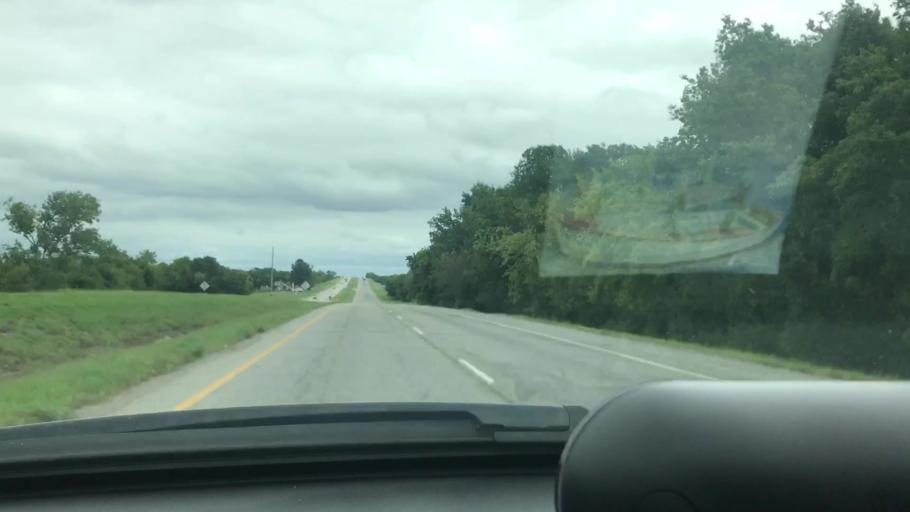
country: US
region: Oklahoma
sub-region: Wagoner County
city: Wagoner
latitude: 35.9697
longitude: -95.3883
